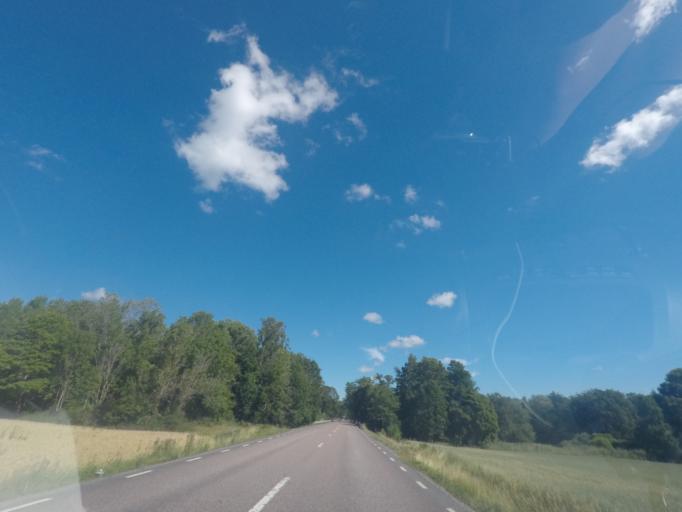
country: SE
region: Uppsala
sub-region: Knivsta Kommun
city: Knivsta
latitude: 59.8802
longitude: 17.9694
